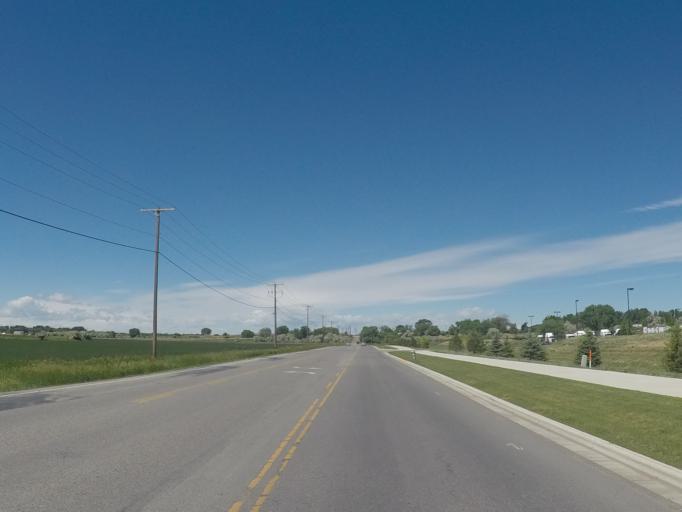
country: US
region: Montana
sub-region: Yellowstone County
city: Billings
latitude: 45.7407
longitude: -108.6076
